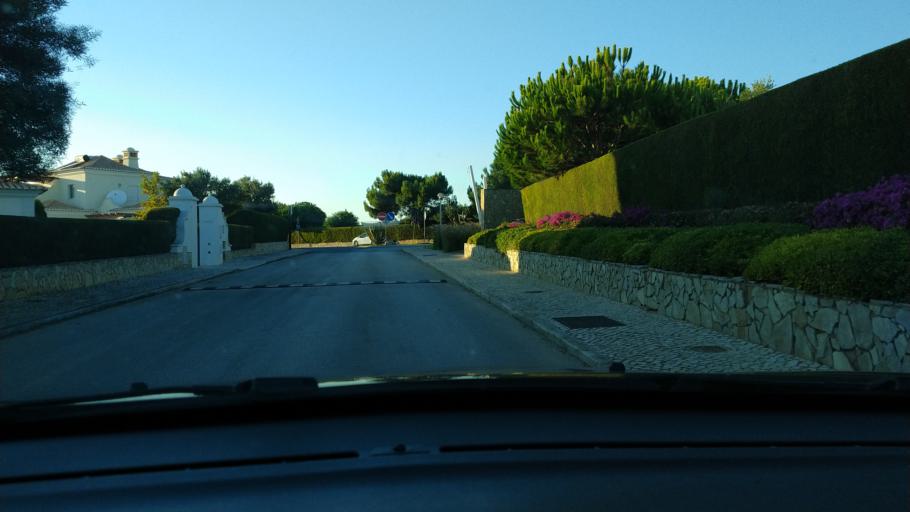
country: PT
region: Faro
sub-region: Vila do Bispo
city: Sagres
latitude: 37.0241
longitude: -8.9294
